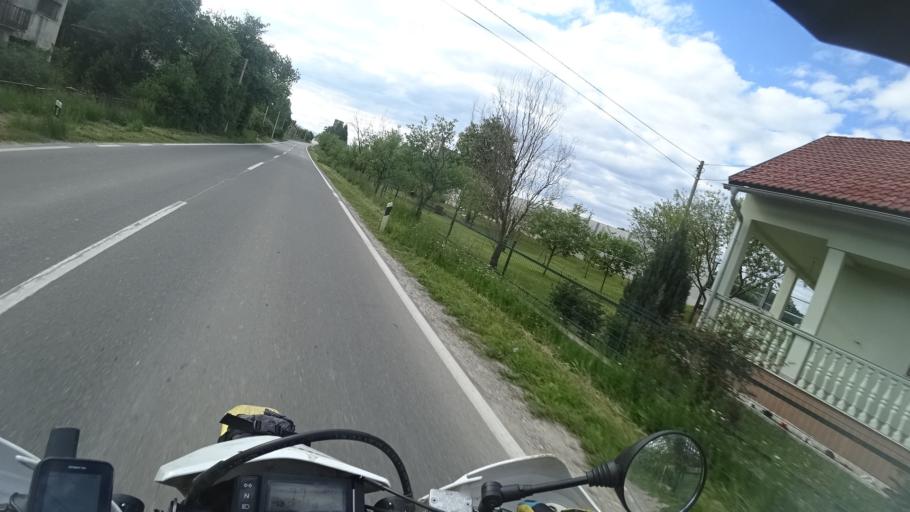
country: HR
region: Licko-Senjska
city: Gospic
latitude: 44.5313
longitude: 15.4012
